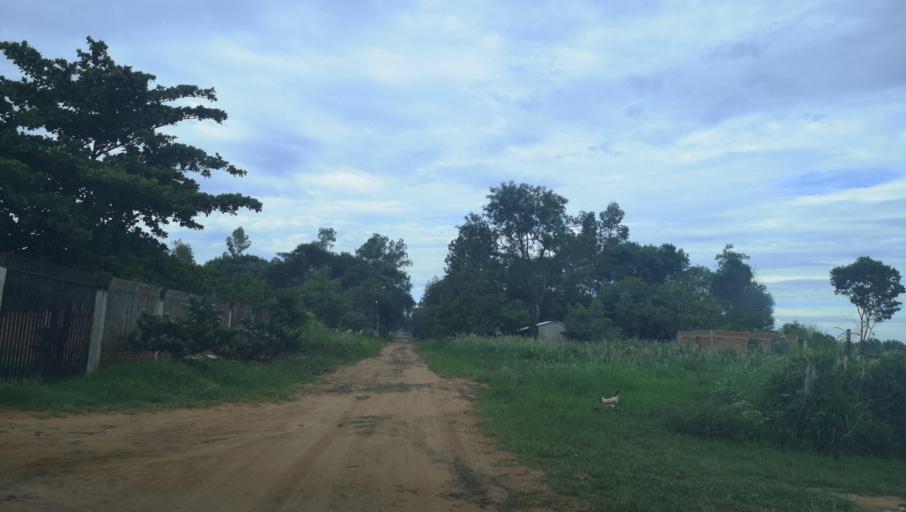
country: PY
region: San Pedro
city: Capiibary
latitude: -24.7364
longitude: -56.0241
